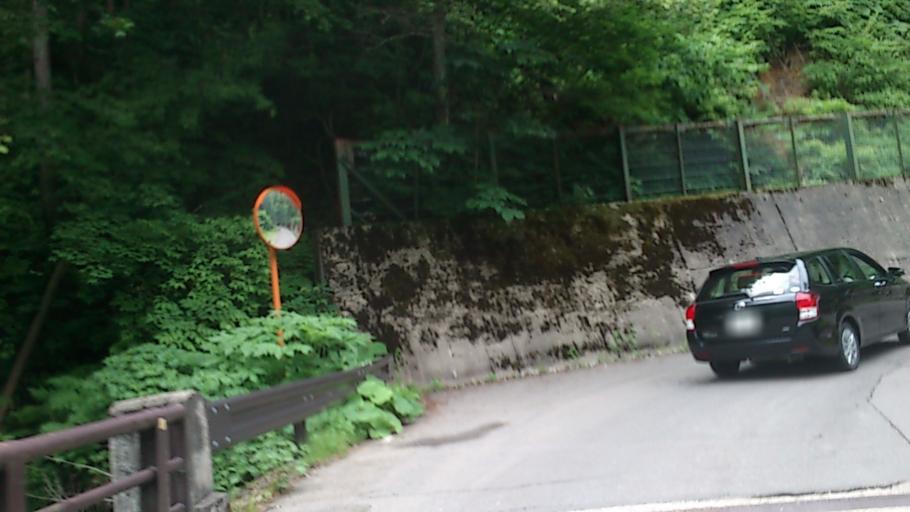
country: JP
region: Aomori
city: Hirosaki
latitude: 40.5160
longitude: 140.1790
